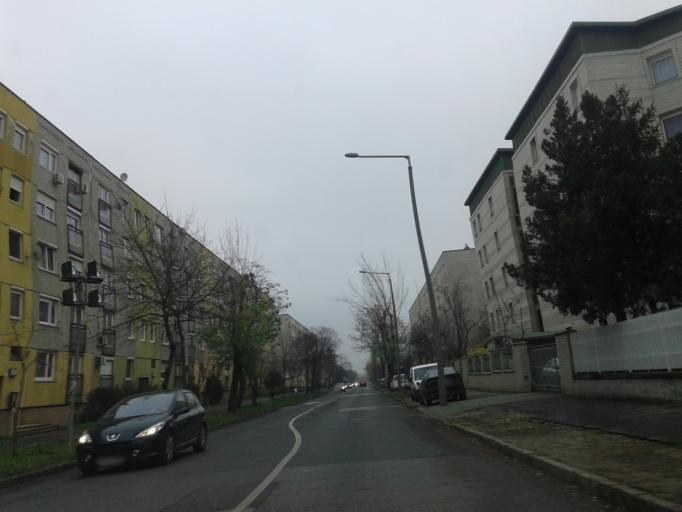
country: HU
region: Budapest
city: Budapest XXI. keruelet
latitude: 47.4302
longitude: 19.0725
